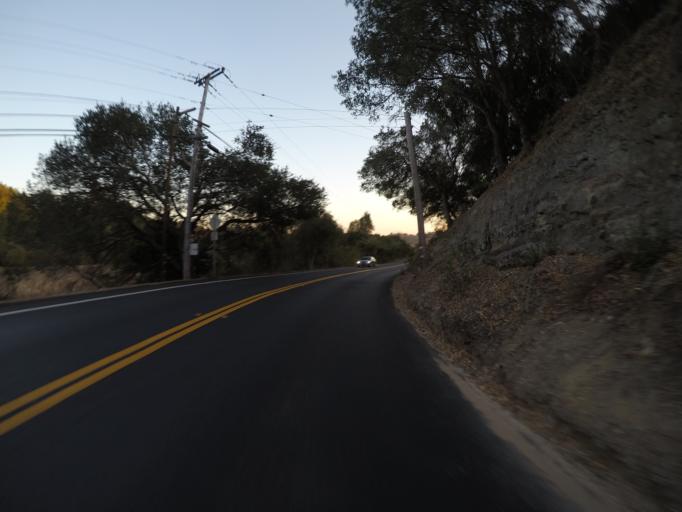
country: US
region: California
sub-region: Santa Cruz County
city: Scotts Valley
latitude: 37.0764
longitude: -122.0040
